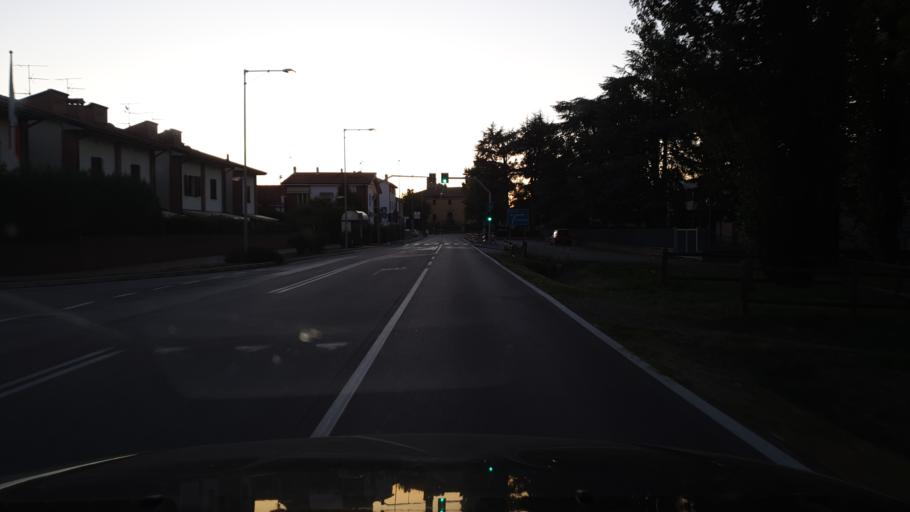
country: IT
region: Emilia-Romagna
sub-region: Provincia di Bologna
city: Altedo
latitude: 44.6620
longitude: 11.4886
